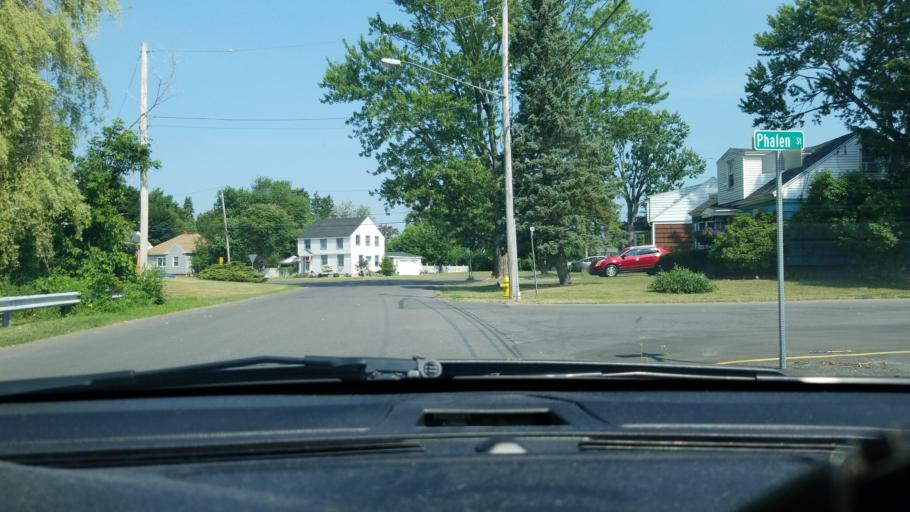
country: US
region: New York
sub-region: Onondaga County
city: Mattydale
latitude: 43.0982
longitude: -76.1469
